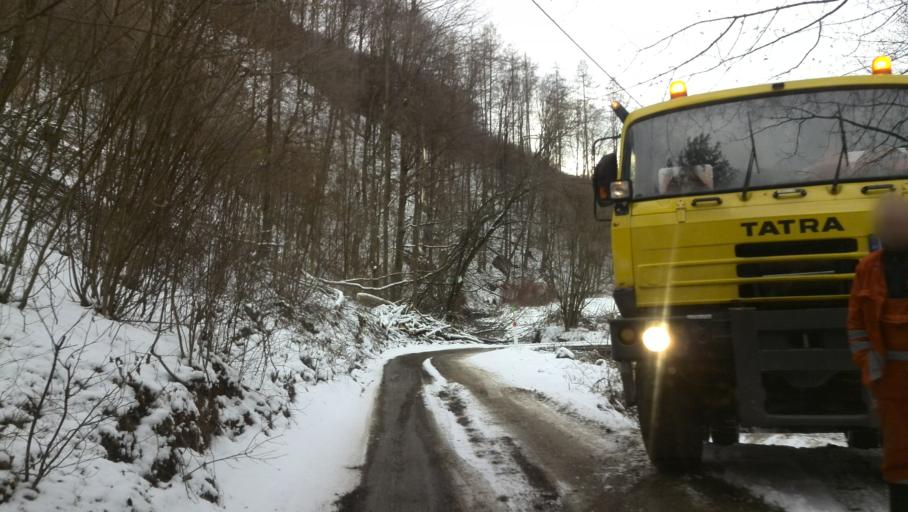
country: SK
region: Kosicky
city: Gelnica
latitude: 48.8117
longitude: 21.0583
